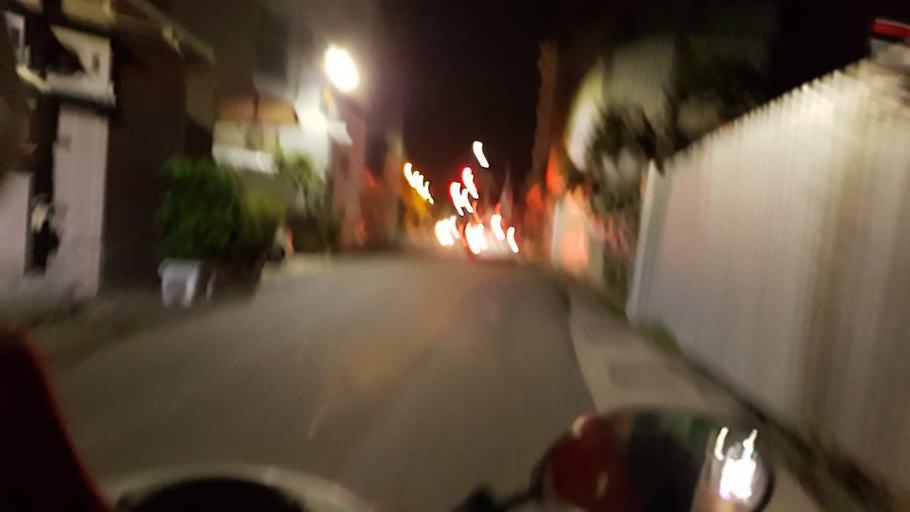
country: TW
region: Taiwan
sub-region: Changhua
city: Chang-hua
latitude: 24.0659
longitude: 120.5261
